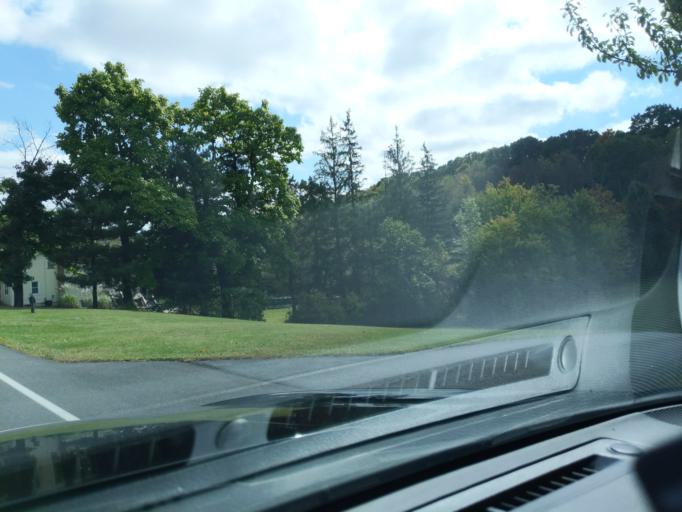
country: US
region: Pennsylvania
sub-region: Blair County
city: Lakemont
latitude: 40.4879
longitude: -78.4277
